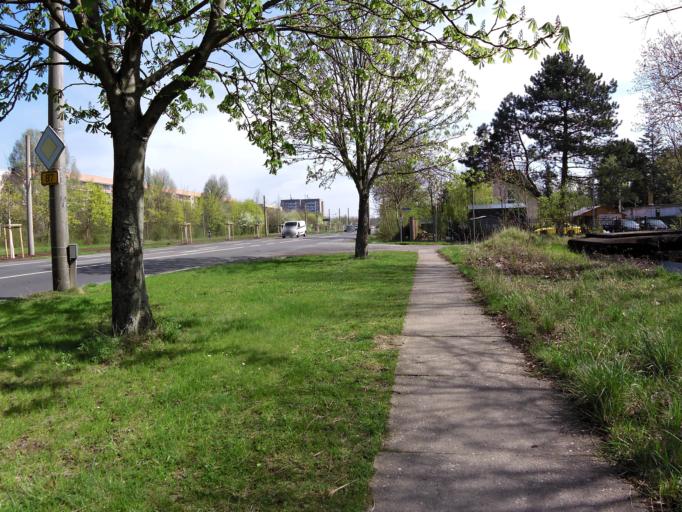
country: DE
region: Saxony
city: Markranstadt
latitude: 51.3171
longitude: 12.2687
